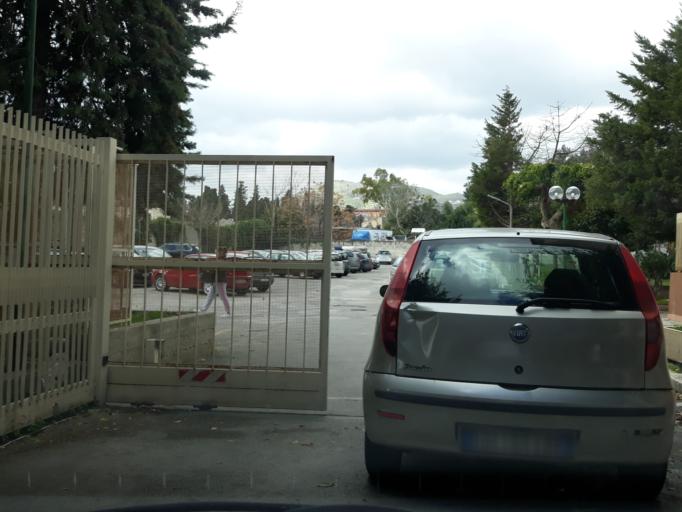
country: IT
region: Sicily
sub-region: Palermo
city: Palermo
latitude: 38.1136
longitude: 13.3409
